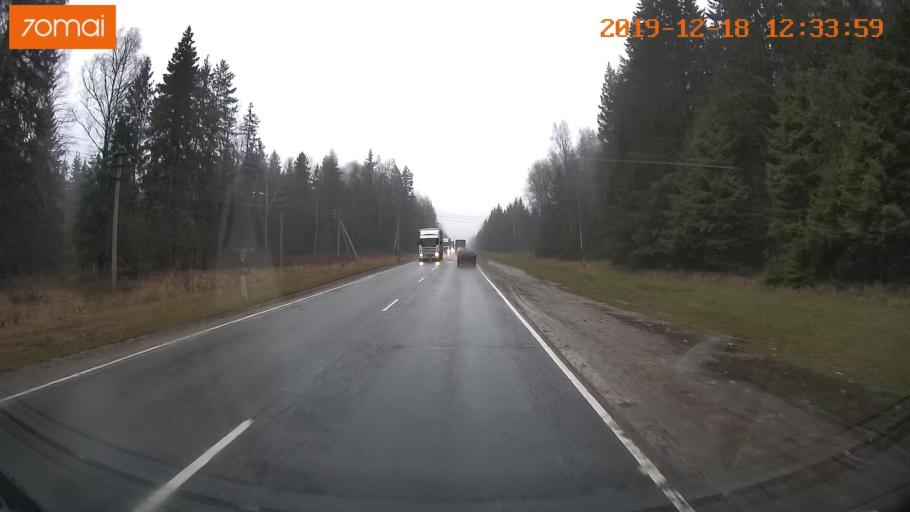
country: RU
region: Moskovskaya
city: Rumyantsevo
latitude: 56.1174
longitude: 36.5671
